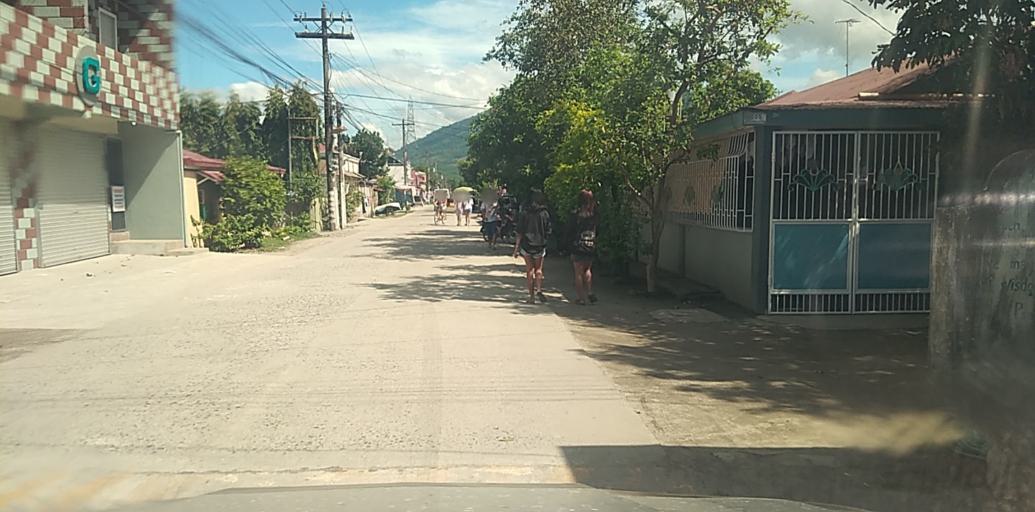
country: PH
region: Central Luzon
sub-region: Province of Pampanga
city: Buensuseso
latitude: 15.1929
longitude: 120.6682
